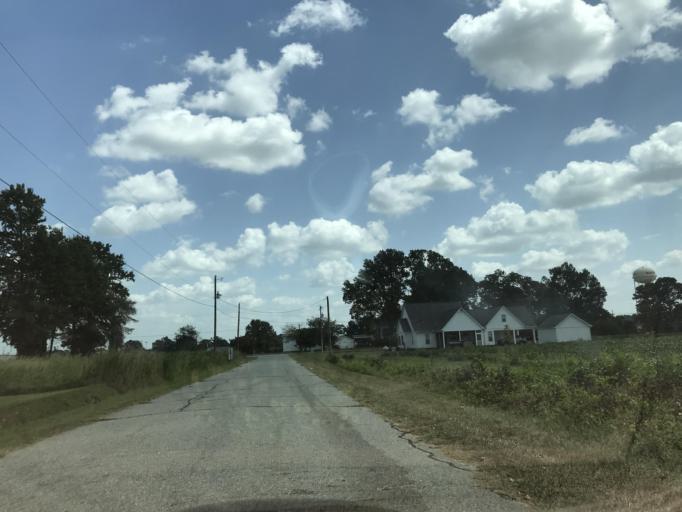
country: US
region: North Carolina
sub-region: Sampson County
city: Plain View
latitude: 35.2480
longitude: -78.3599
